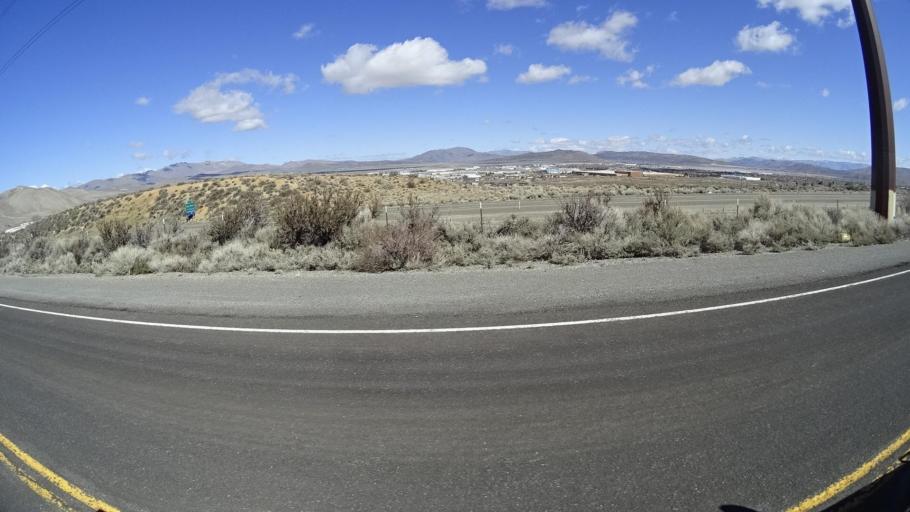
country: US
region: Nevada
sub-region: Washoe County
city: Lemmon Valley
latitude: 39.6222
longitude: -119.8999
